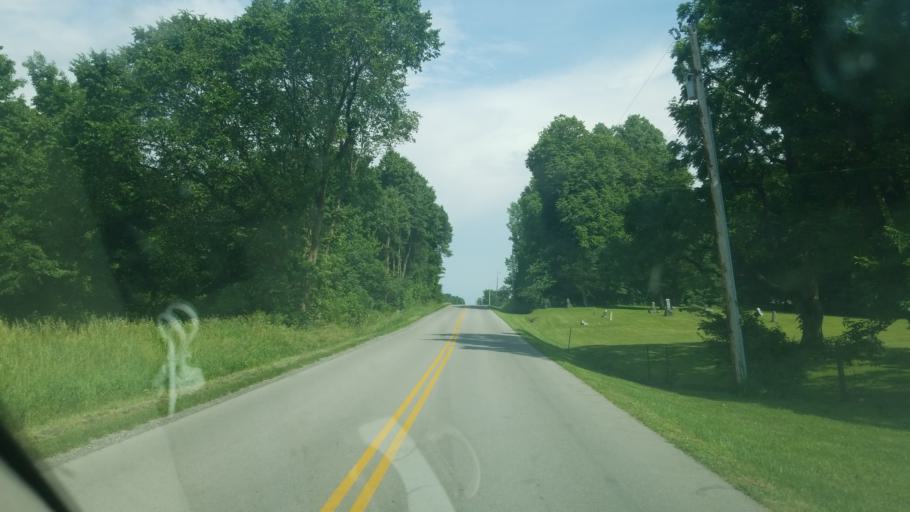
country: US
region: Ohio
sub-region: Logan County
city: West Liberty
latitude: 40.2988
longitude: -83.6503
